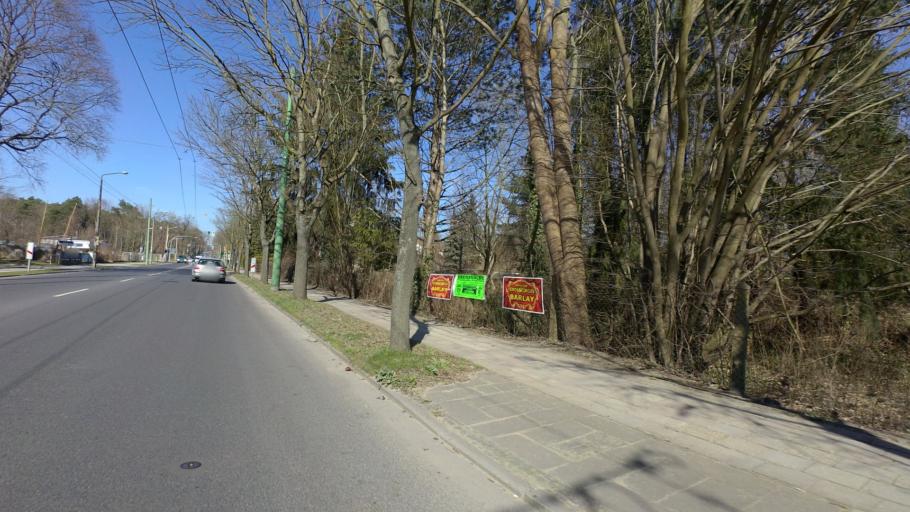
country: DE
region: Brandenburg
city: Eberswalde
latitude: 52.8416
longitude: 13.8211
